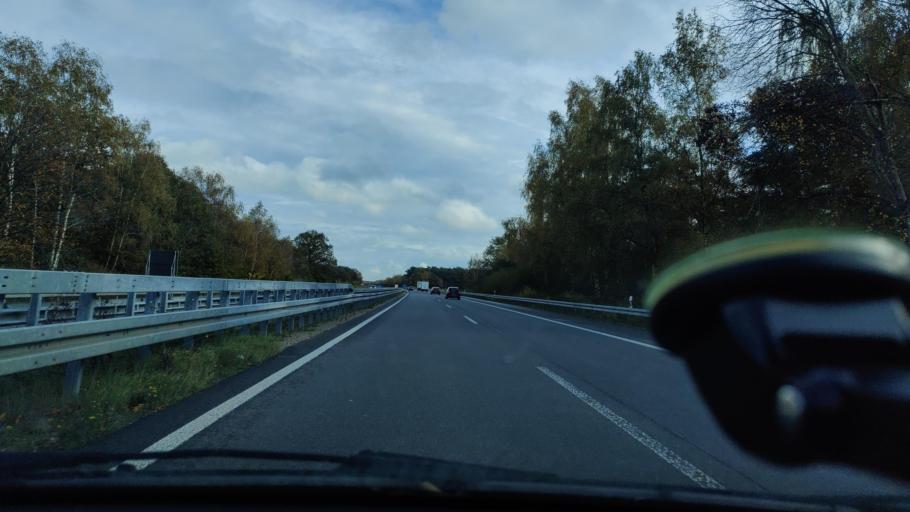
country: DE
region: North Rhine-Westphalia
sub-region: Regierungsbezirk Dusseldorf
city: Issum
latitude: 51.5663
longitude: 6.4662
